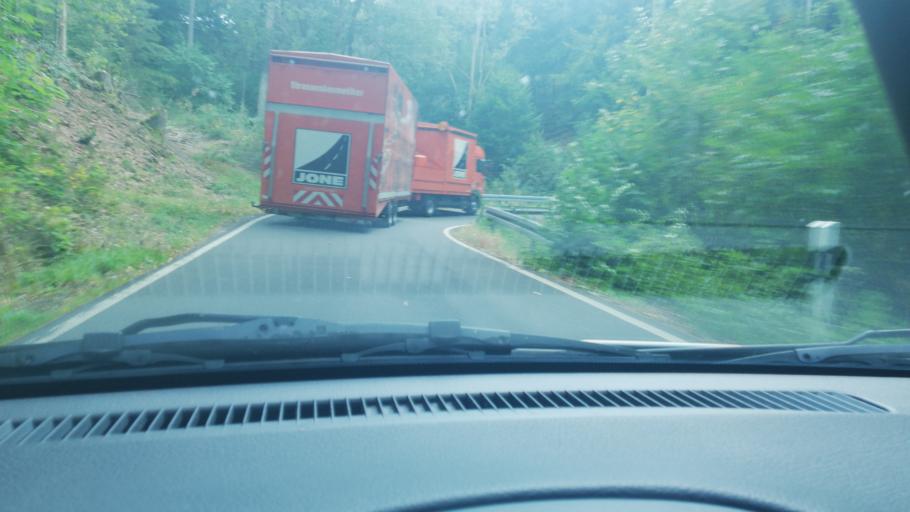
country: DE
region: Bavaria
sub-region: Regierungsbezirk Unterfranken
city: Wiesen
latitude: 50.1437
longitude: 9.3429
